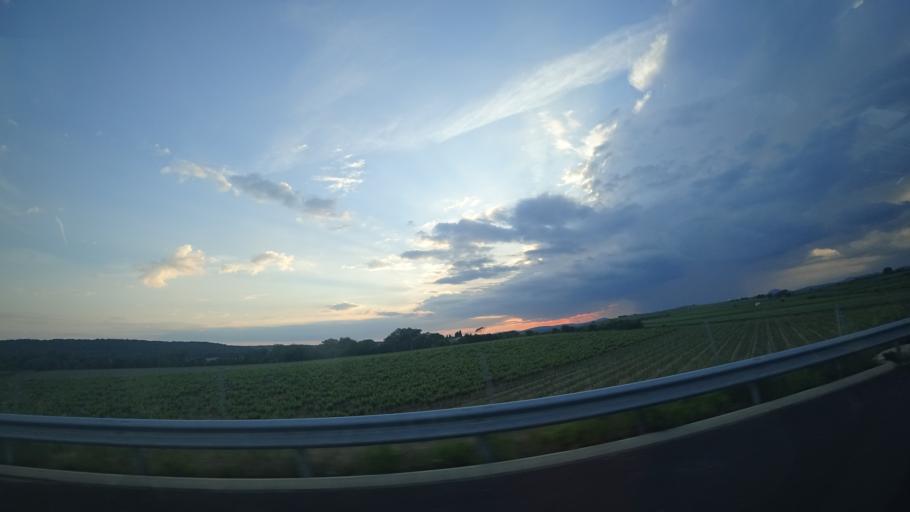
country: FR
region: Languedoc-Roussillon
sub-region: Departement de l'Herault
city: Lezignan-la-Cebe
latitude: 43.5148
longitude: 3.4432
